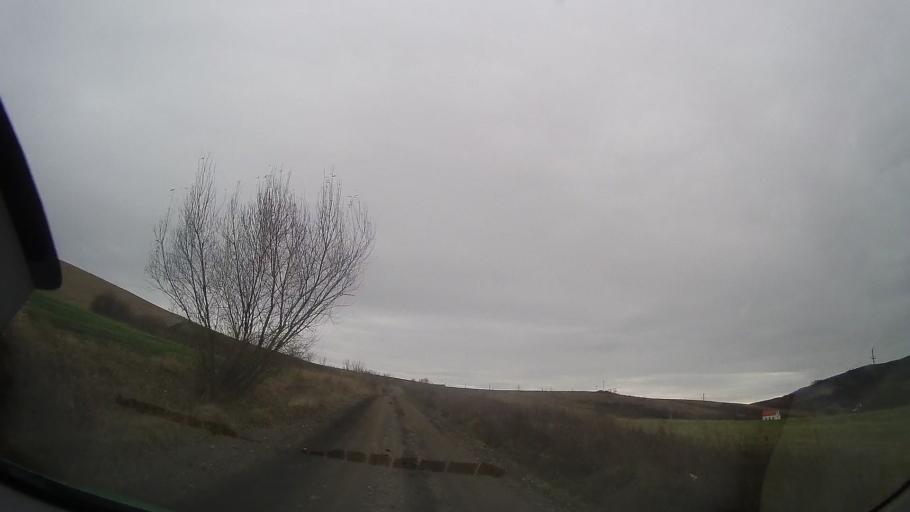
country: RO
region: Mures
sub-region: Comuna Bala
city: Bala
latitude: 46.6958
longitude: 24.4899
